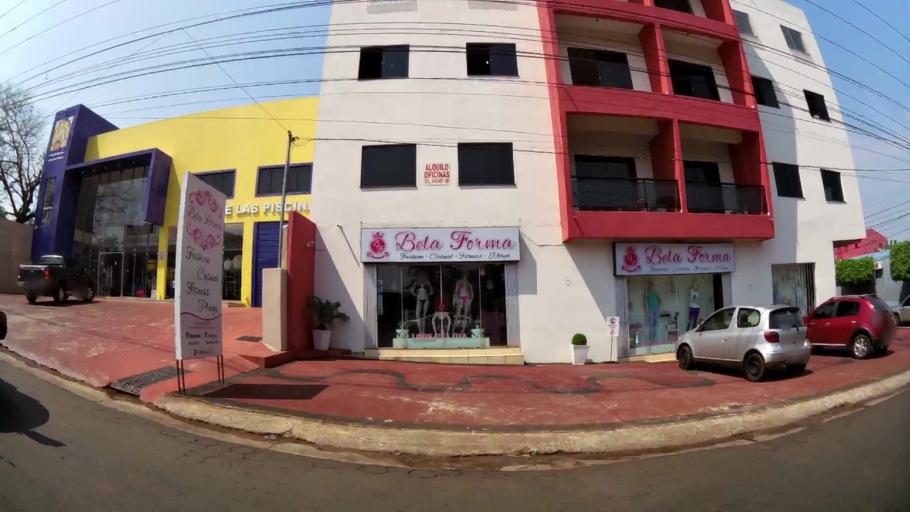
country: PY
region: Alto Parana
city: Presidente Franco
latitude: -25.5249
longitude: -54.6249
